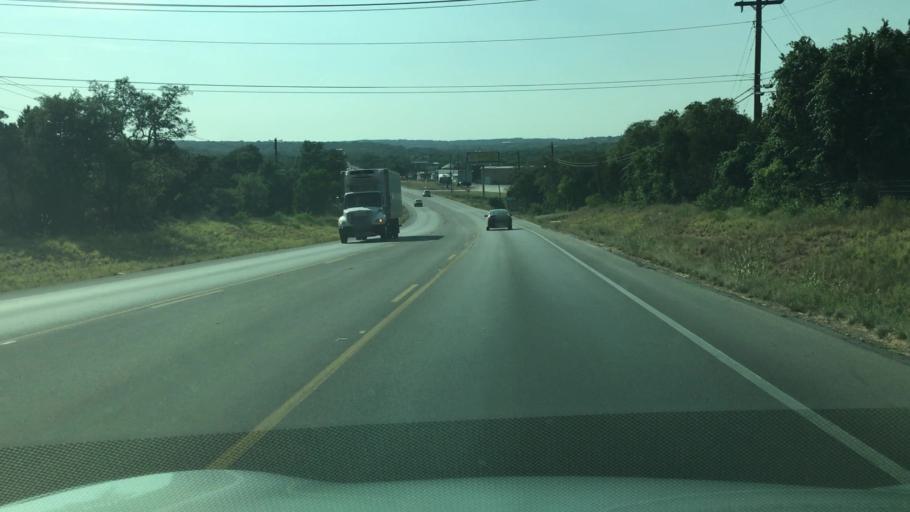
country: US
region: Texas
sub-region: Hays County
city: Wimberley
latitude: 29.9280
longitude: -98.0677
